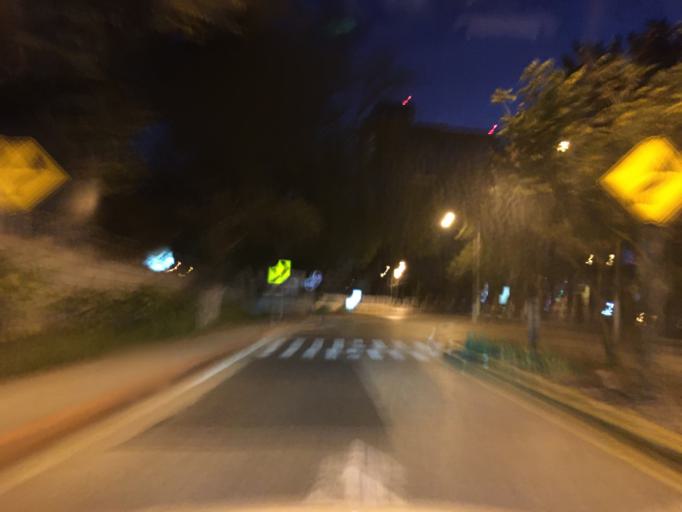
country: GT
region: Guatemala
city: Guatemala City
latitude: 14.6130
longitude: -90.5096
